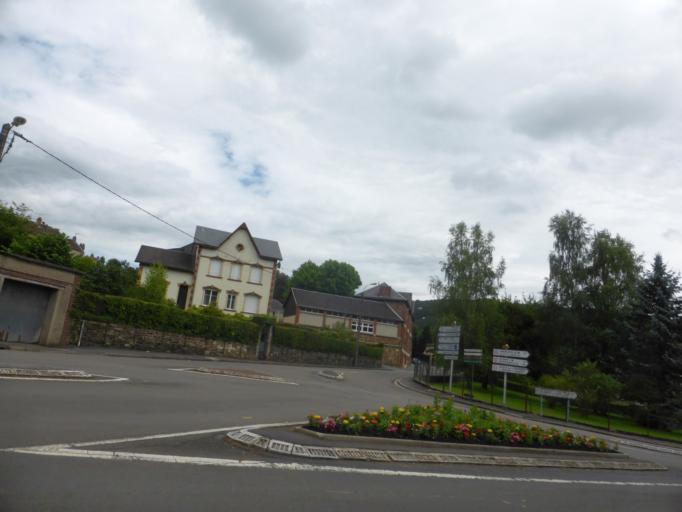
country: FR
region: Champagne-Ardenne
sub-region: Departement des Ardennes
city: Montherme
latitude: 49.8843
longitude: 4.7404
